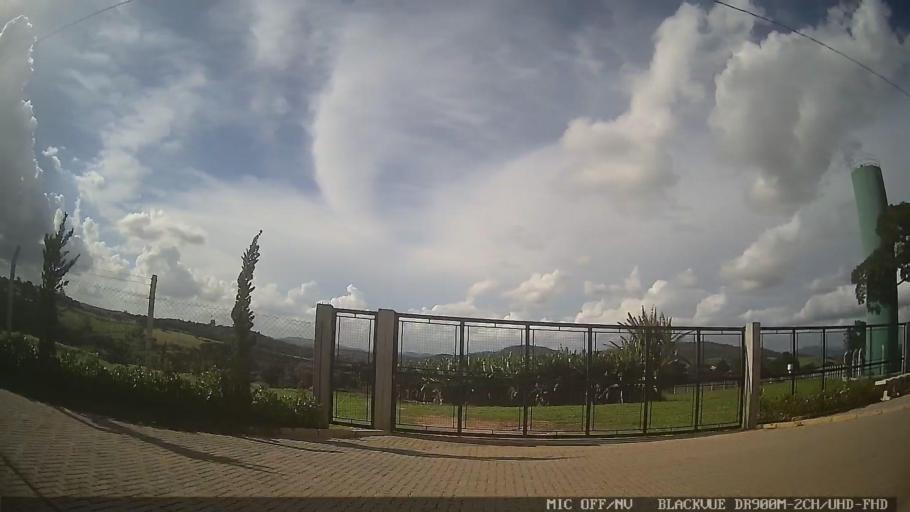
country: BR
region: Sao Paulo
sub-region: Bom Jesus Dos Perdoes
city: Bom Jesus dos Perdoes
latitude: -23.1227
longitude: -46.4895
